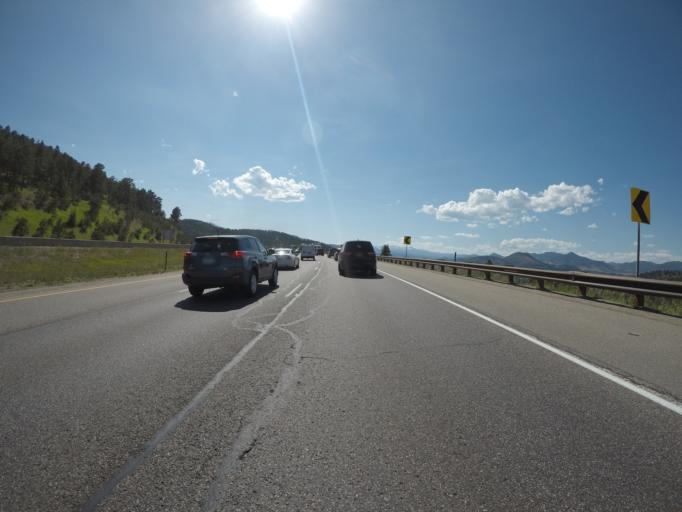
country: US
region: Colorado
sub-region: Jefferson County
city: Genesee
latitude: 39.7143
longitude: -105.3103
